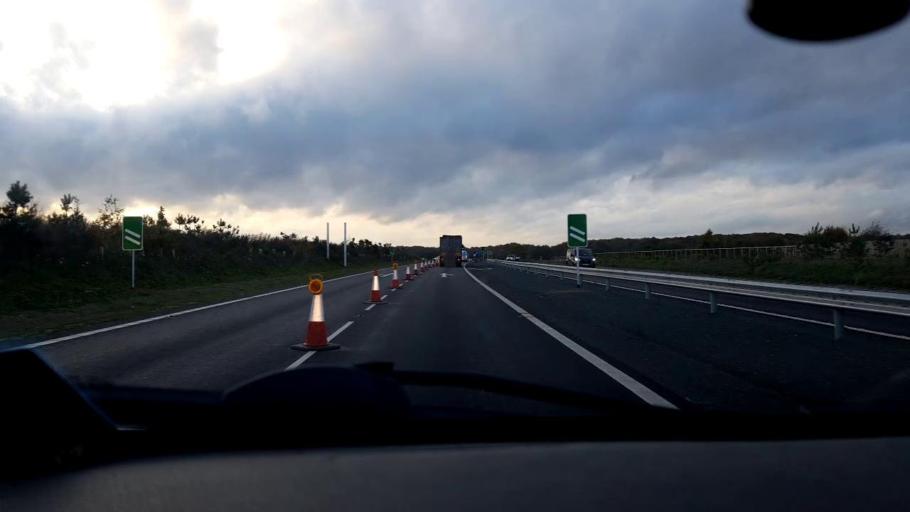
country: GB
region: England
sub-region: Norfolk
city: Costessey
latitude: 52.6960
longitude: 1.1973
